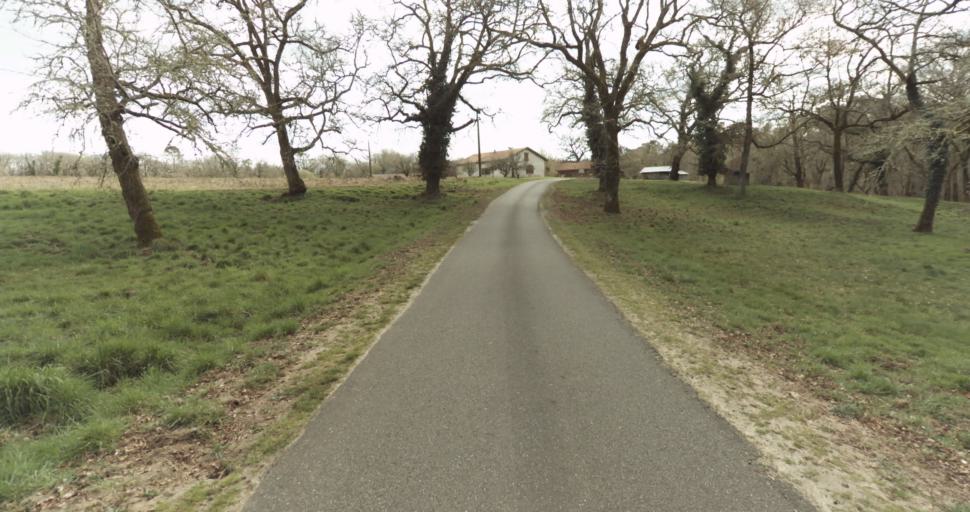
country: FR
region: Aquitaine
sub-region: Departement des Landes
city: Roquefort
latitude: 44.0433
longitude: -0.4251
